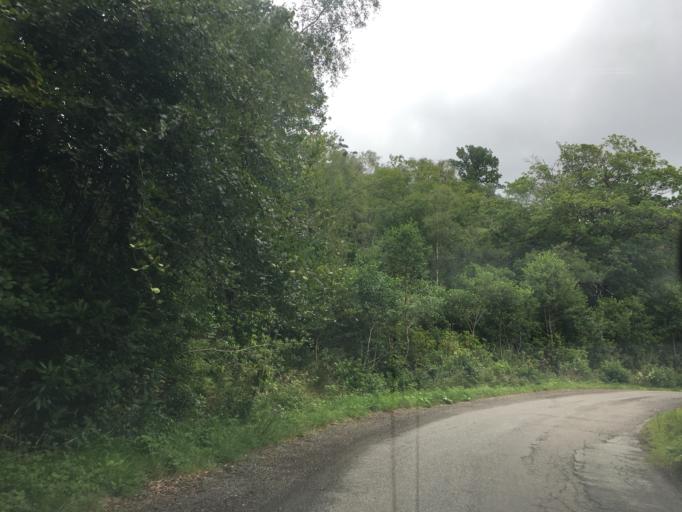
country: GB
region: Scotland
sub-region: Argyll and Bute
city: Oban
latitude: 56.2875
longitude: -5.3126
